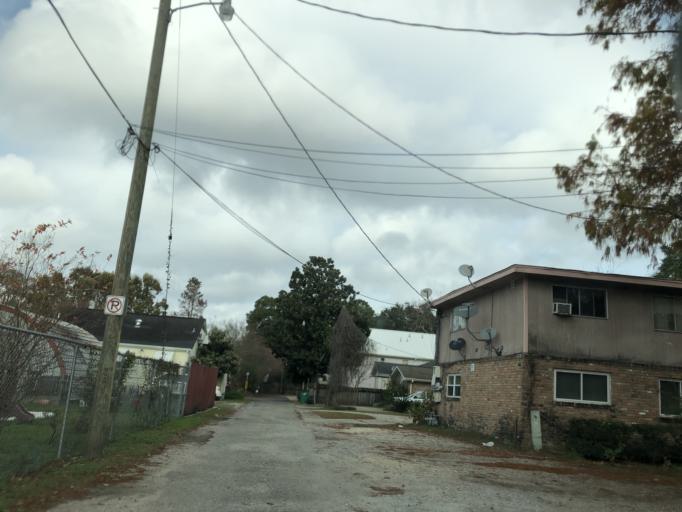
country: US
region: Louisiana
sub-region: Jefferson Parish
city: Metairie Terrace
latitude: 29.9767
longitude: -90.1593
